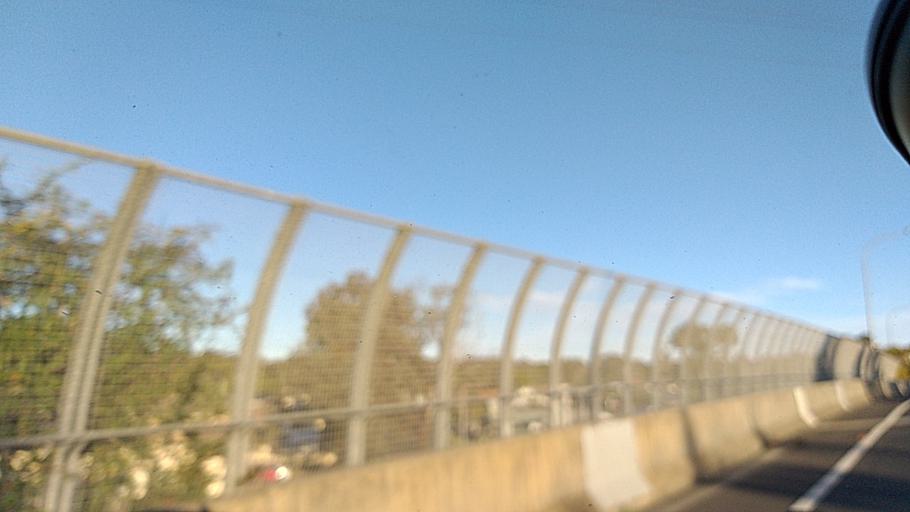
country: AU
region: New South Wales
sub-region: Campbelltown Municipality
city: Leumeah
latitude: -34.0555
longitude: 150.8240
